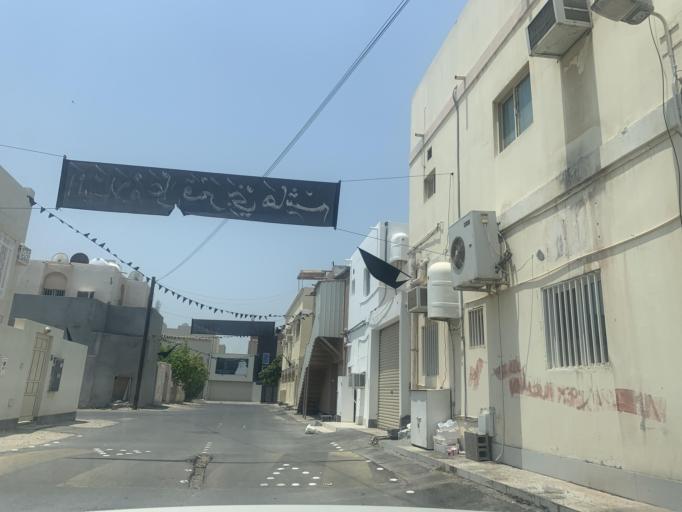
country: BH
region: Central Governorate
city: Madinat Hamad
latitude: 26.1430
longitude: 50.4613
